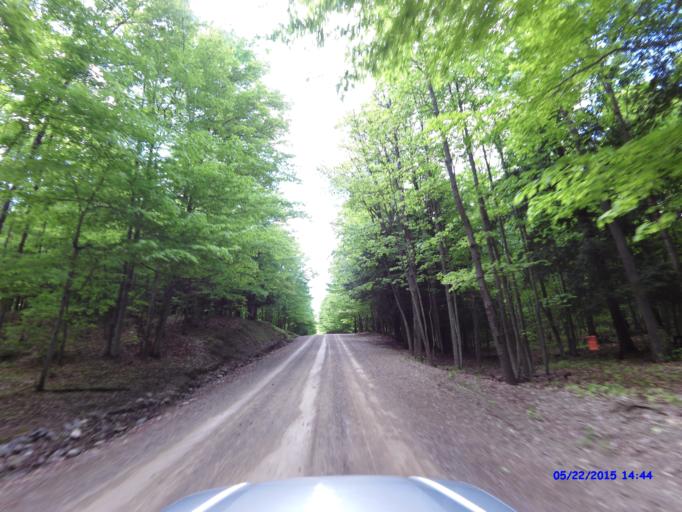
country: US
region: New York
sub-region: Cattaraugus County
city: Franklinville
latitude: 42.3569
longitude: -78.5697
